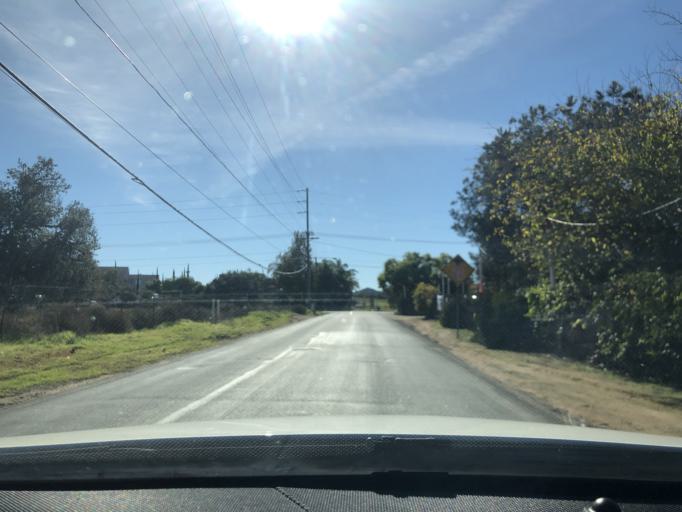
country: US
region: California
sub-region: San Diego County
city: Escondido
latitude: 33.0929
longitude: -117.0799
